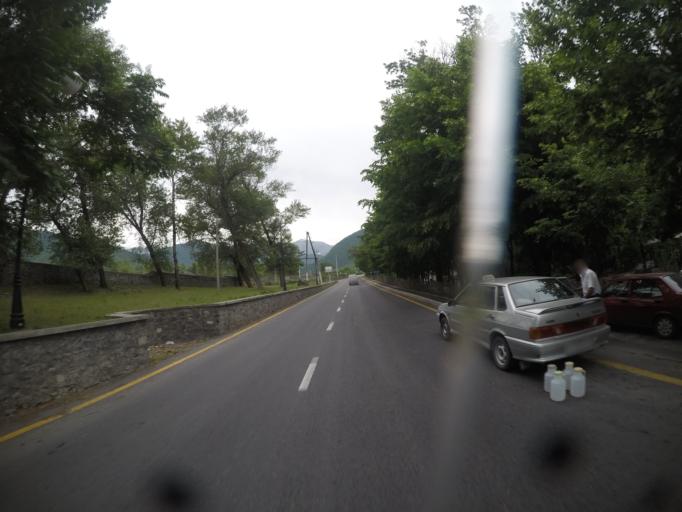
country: AZ
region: Shaki City
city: Sheki
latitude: 41.2415
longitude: 47.1865
